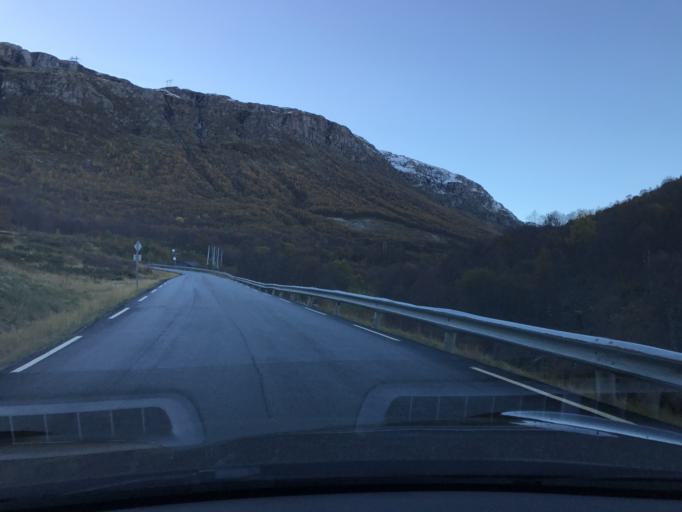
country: NO
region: Sogn og Fjordane
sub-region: Aurland
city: Aurlandsvangen
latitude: 60.8491
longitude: 7.3099
